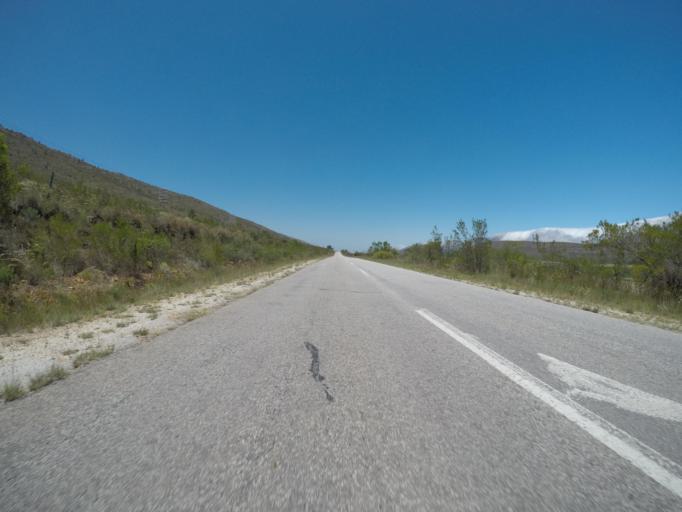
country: ZA
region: Eastern Cape
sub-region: Cacadu District Municipality
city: Kareedouw
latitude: -33.8372
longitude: 23.9202
